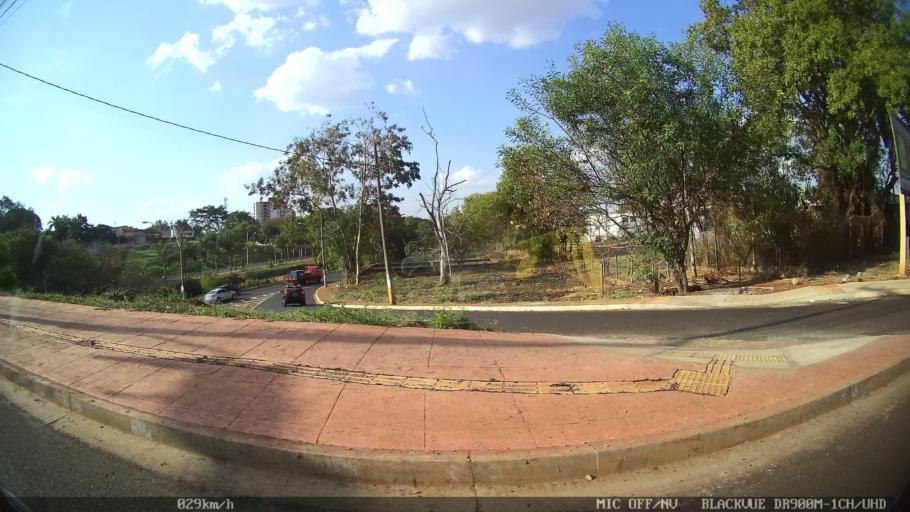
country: BR
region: Sao Paulo
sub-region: Ribeirao Preto
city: Ribeirao Preto
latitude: -21.1607
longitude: -47.8132
